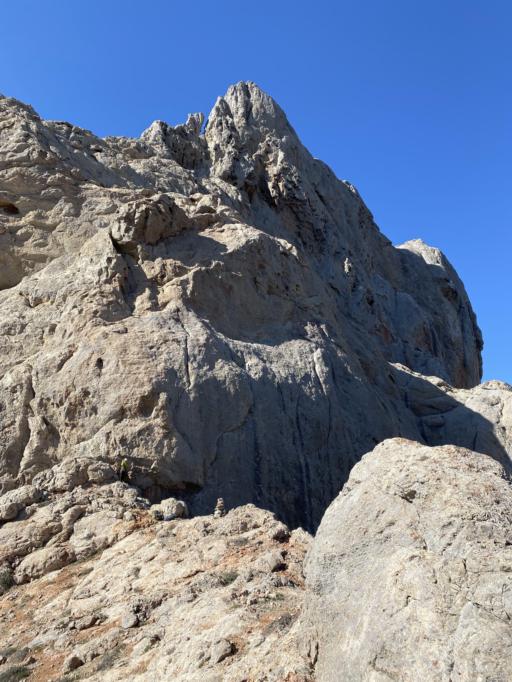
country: KZ
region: Ongtustik Qazaqstan
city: Ashchysay
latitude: 43.7624
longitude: 68.7838
